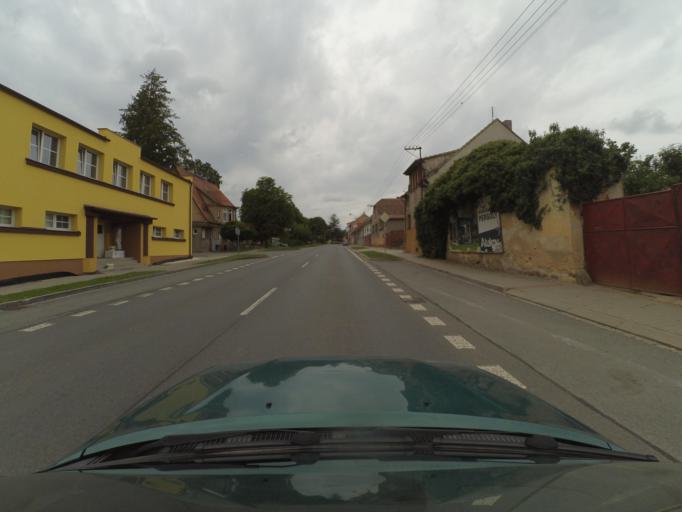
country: CZ
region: Plzensky
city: Kozlany
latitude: 49.9949
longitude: 13.5434
